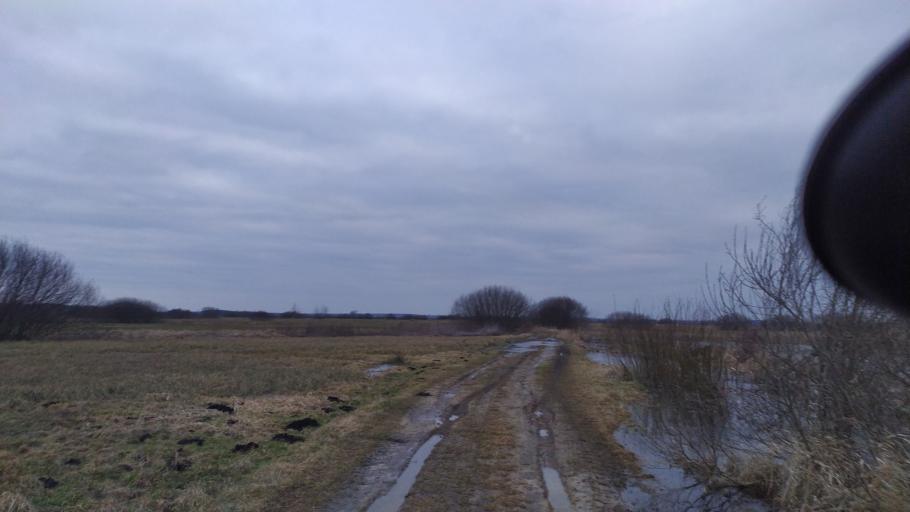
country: PL
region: Lublin Voivodeship
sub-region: Powiat lubartowski
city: Abramow
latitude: 51.4301
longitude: 22.3250
